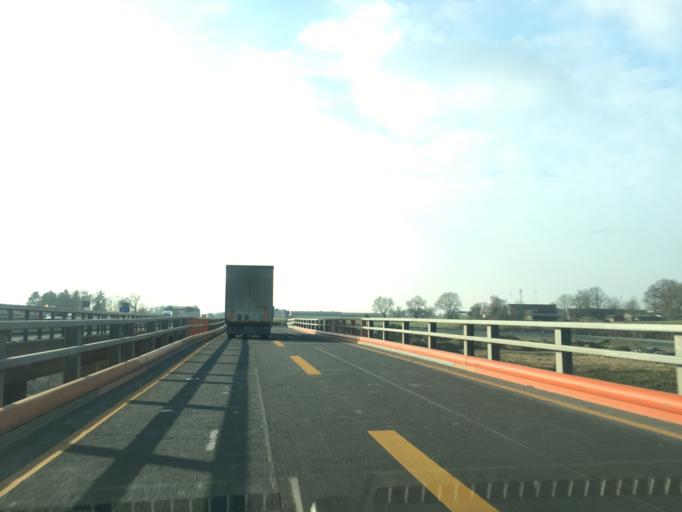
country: DE
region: North Rhine-Westphalia
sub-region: Regierungsbezirk Munster
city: Lotte
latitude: 52.2684
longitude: 7.9276
